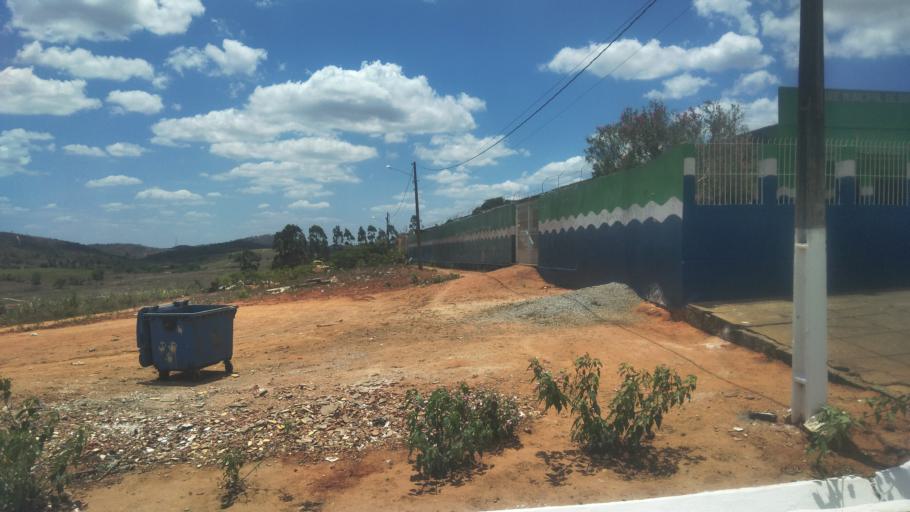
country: BR
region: Pernambuco
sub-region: Vicencia
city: Vicencia
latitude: -7.7272
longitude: -35.3241
